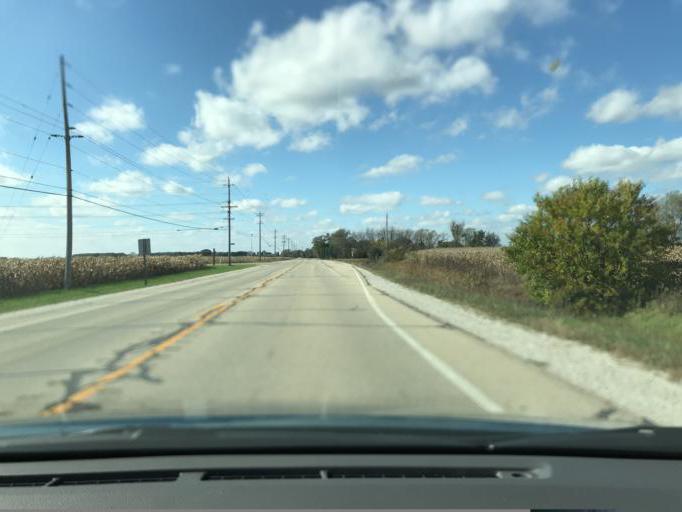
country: US
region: Wisconsin
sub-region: Kenosha County
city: Somers
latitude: 42.6250
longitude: -87.9906
